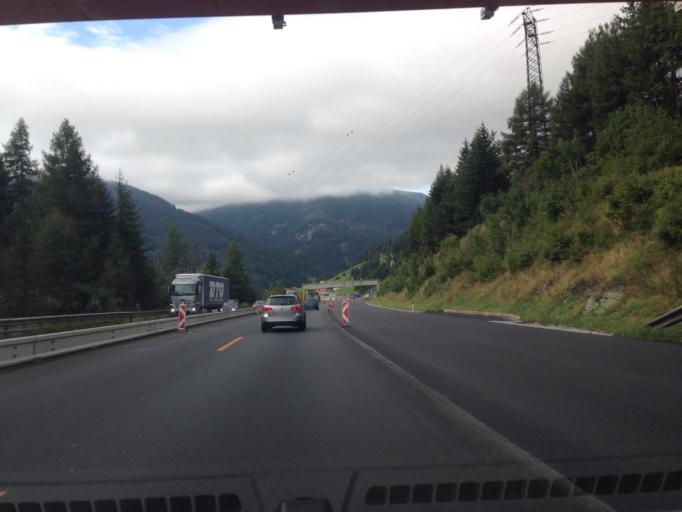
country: AT
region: Tyrol
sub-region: Politischer Bezirk Innsbruck Land
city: Gries am Brenner
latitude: 47.0457
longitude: 11.4804
